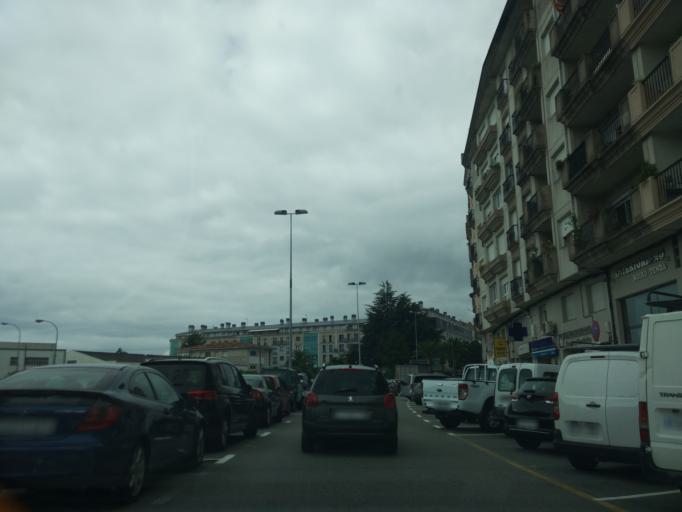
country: ES
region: Galicia
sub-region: Provincia da Coruna
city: Boiro
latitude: 42.6469
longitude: -8.8799
